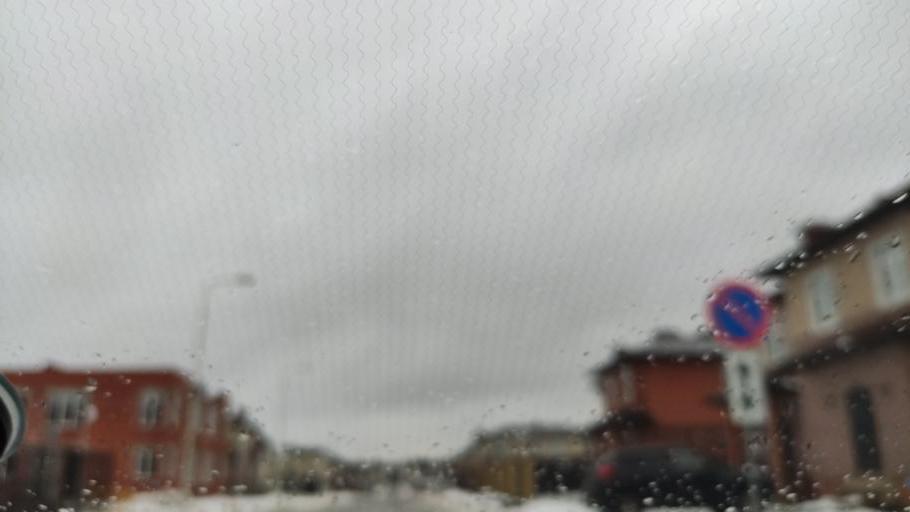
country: RU
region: Moskovskaya
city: Vatutinki
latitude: 55.4262
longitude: 37.3813
